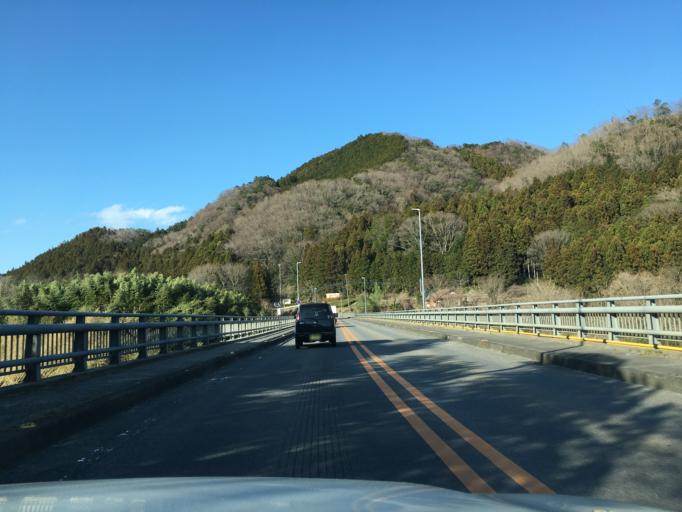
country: JP
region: Ibaraki
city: Omiya
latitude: 36.6554
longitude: 140.3930
